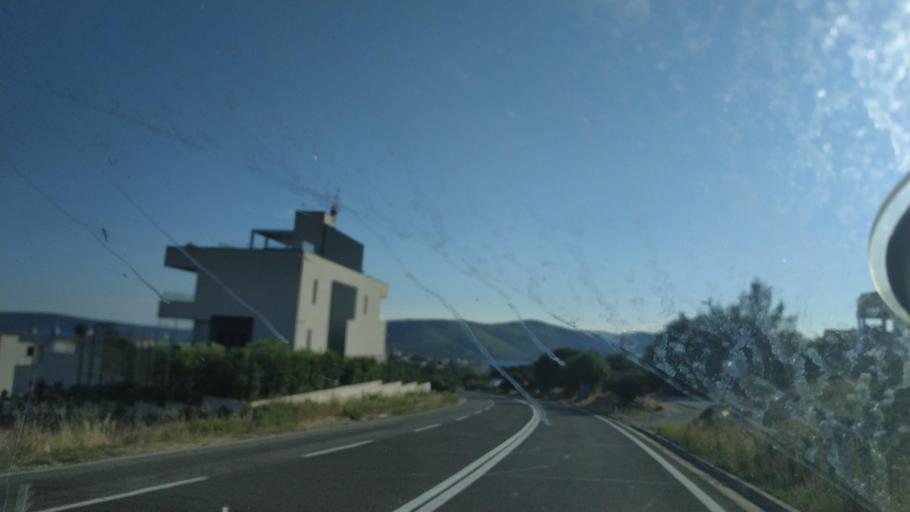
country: HR
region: Splitsko-Dalmatinska
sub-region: Grad Trogir
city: Trogir
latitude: 43.5158
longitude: 16.1959
